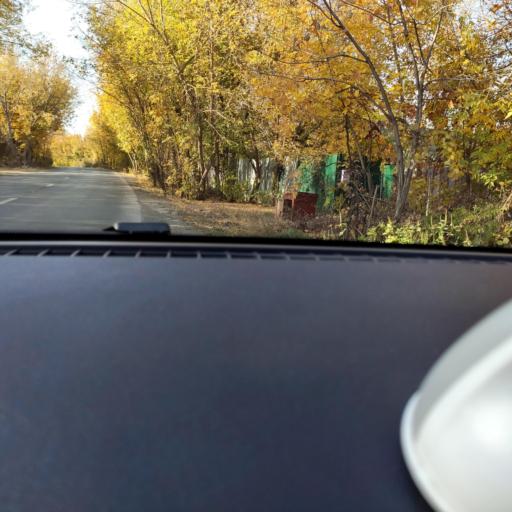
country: RU
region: Samara
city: Smyshlyayevka
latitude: 53.2412
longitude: 50.3511
